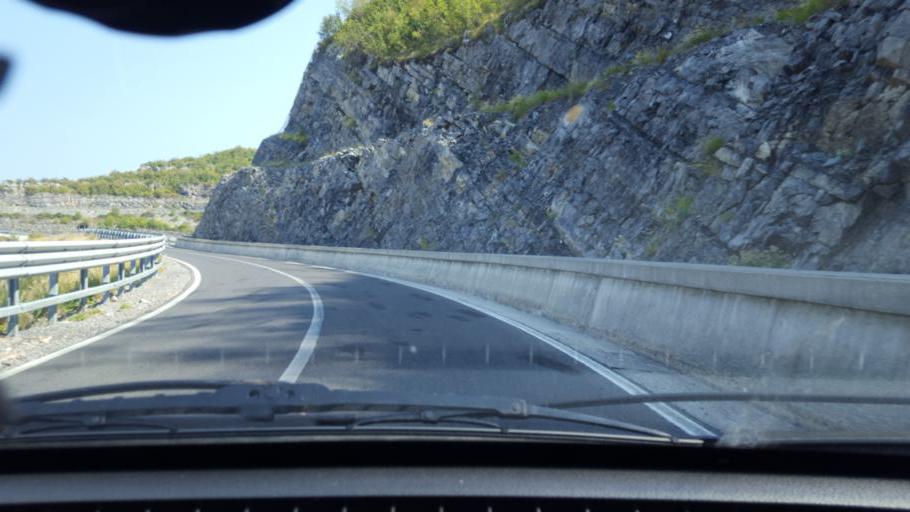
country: AL
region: Shkoder
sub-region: Rrethi i Malesia e Madhe
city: Kastrat
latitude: 42.4132
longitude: 19.5000
